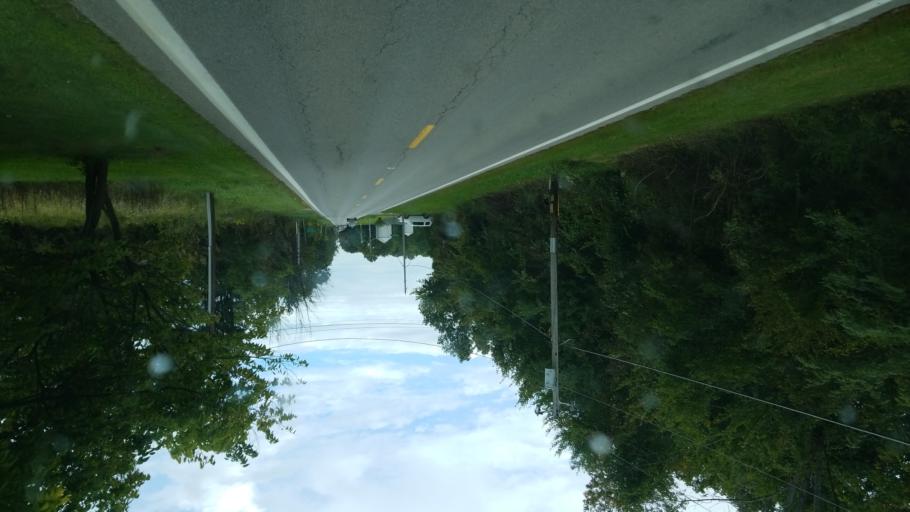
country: US
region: Ohio
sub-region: Franklin County
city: New Albany
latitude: 40.1518
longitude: -82.8084
